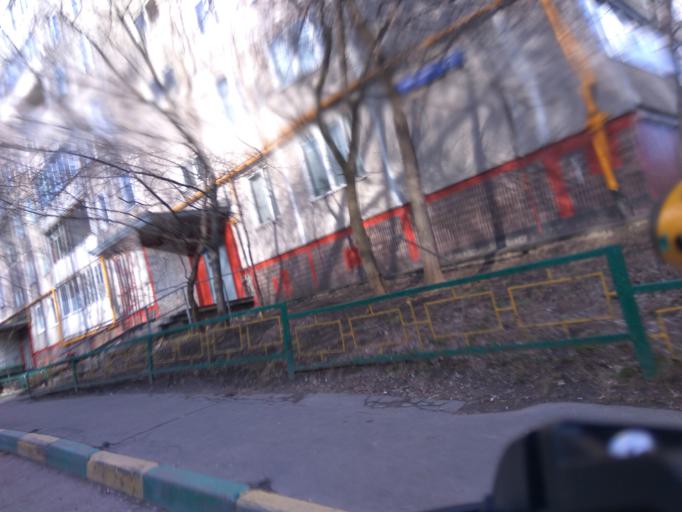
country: RU
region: Moscow
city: Davydkovo
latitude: 55.7245
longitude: 37.4778
